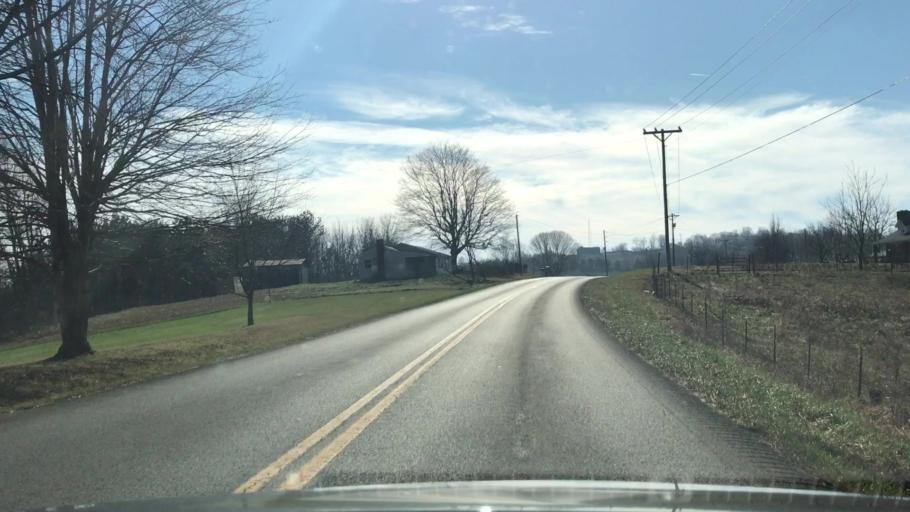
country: US
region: Kentucky
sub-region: Metcalfe County
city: Edmonton
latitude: 36.8895
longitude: -85.6631
